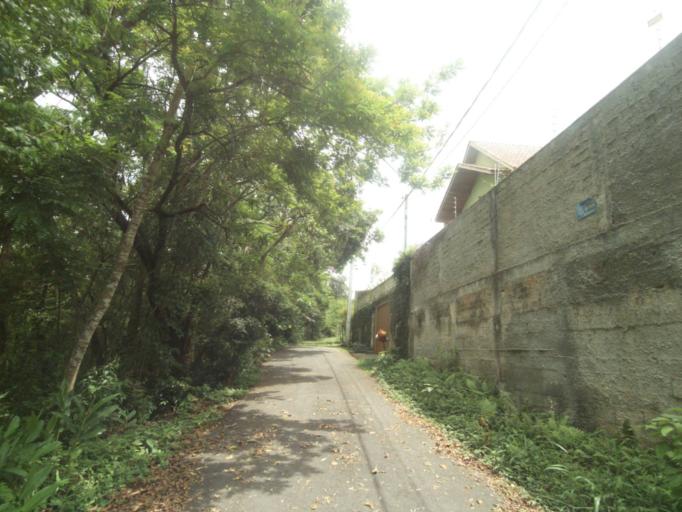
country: BR
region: Parana
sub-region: Curitiba
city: Curitiba
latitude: -25.3894
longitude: -49.2784
